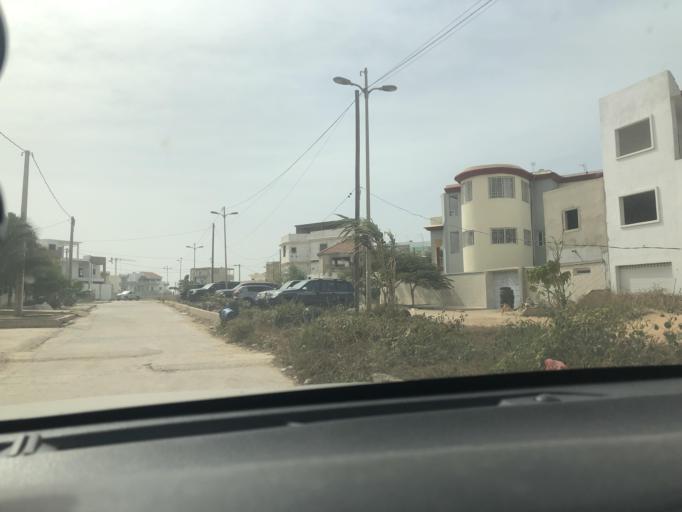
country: SN
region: Dakar
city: Mermoz Boabab
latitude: 14.7331
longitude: -17.5011
